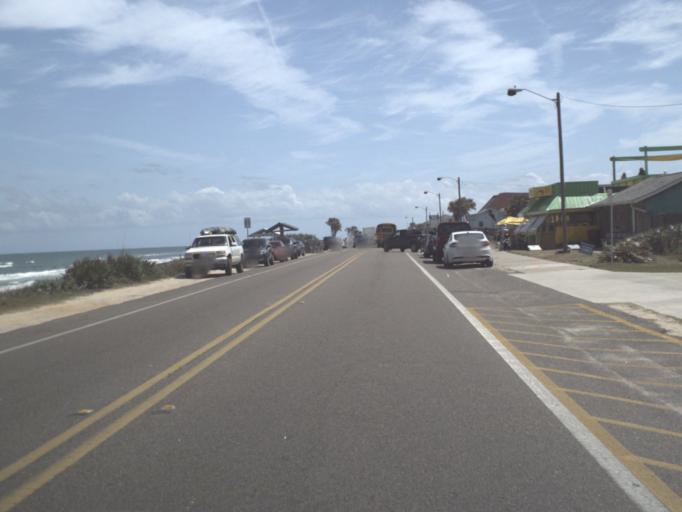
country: US
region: Florida
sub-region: Flagler County
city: Flagler Beach
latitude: 29.4885
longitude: -81.1311
